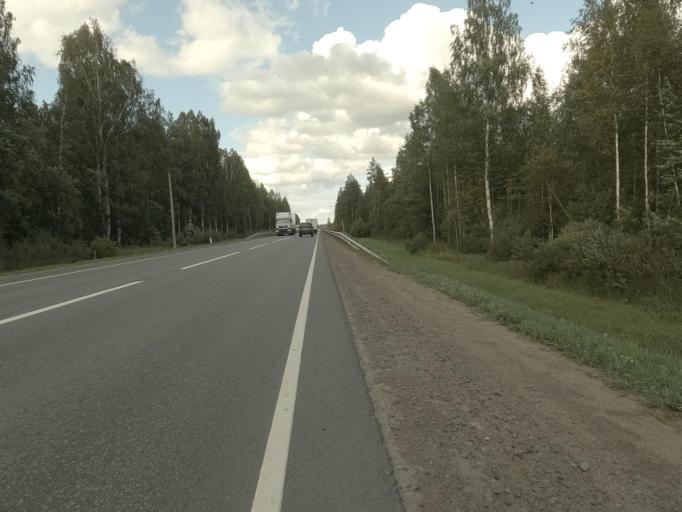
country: RU
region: Leningrad
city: Mga
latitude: 59.7401
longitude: 31.0769
